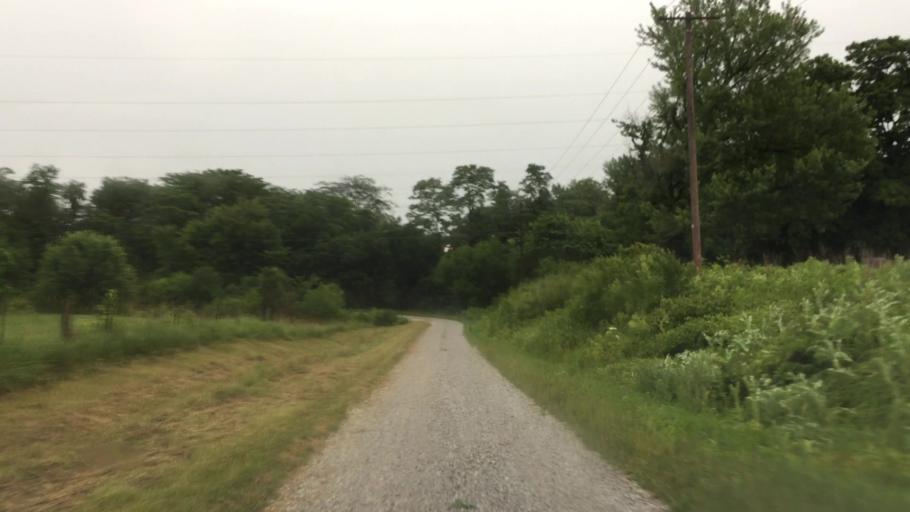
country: US
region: Illinois
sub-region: Hancock County
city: Nauvoo
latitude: 40.5493
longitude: -91.3527
